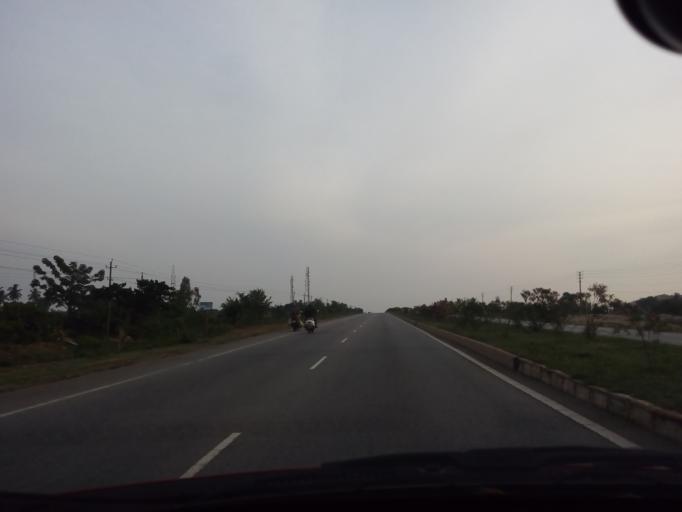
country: IN
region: Karnataka
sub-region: Chikkaballapur
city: Chik Ballapur
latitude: 13.5217
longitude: 77.7649
